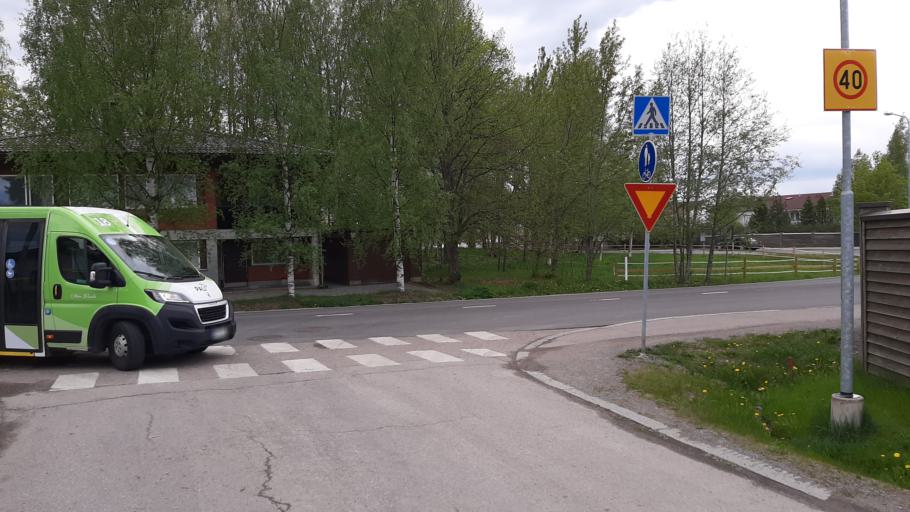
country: FI
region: Pirkanmaa
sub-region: Tampere
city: Tampere
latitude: 61.4727
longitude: 23.8134
